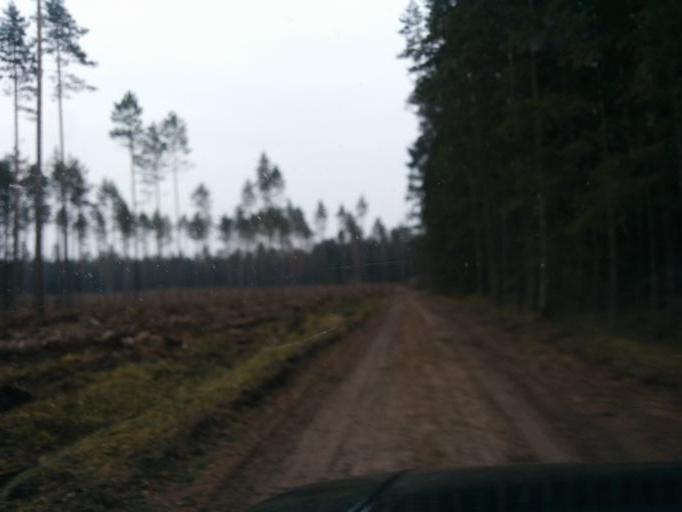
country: LV
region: Ikskile
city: Ikskile
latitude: 56.8057
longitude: 24.4829
